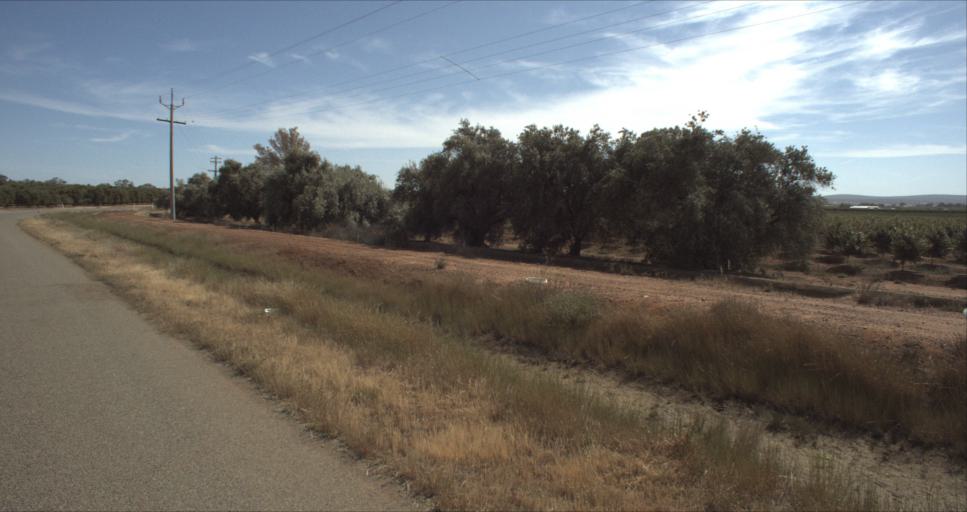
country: AU
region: New South Wales
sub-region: Leeton
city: Leeton
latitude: -34.5882
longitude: 146.4616
